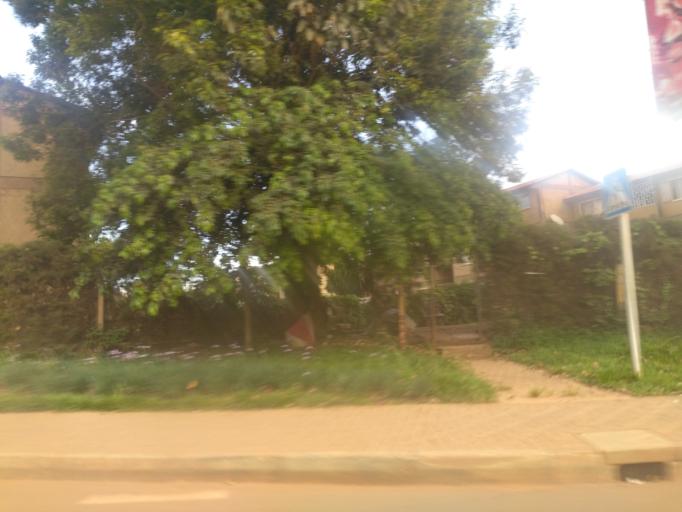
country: UG
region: Central Region
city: Kampala Central Division
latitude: 0.3443
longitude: 32.5962
